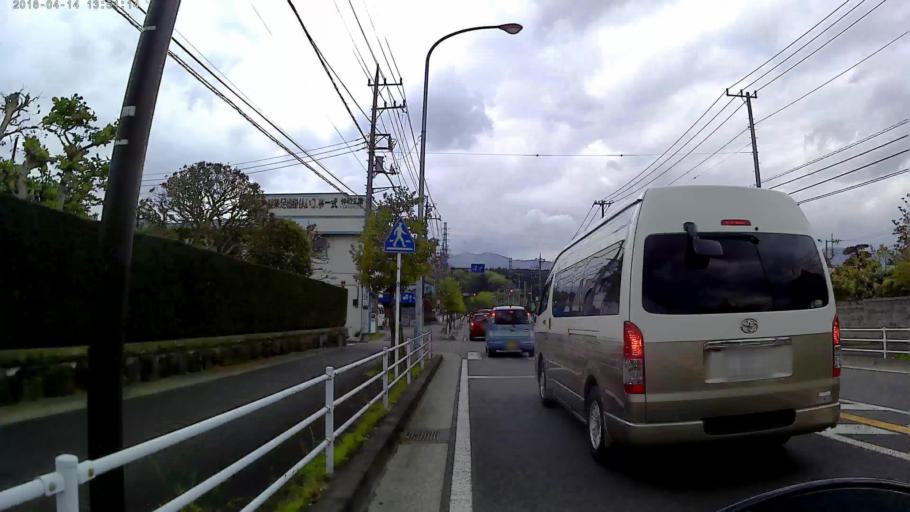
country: JP
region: Kanagawa
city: Odawara
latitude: 35.3254
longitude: 139.1140
